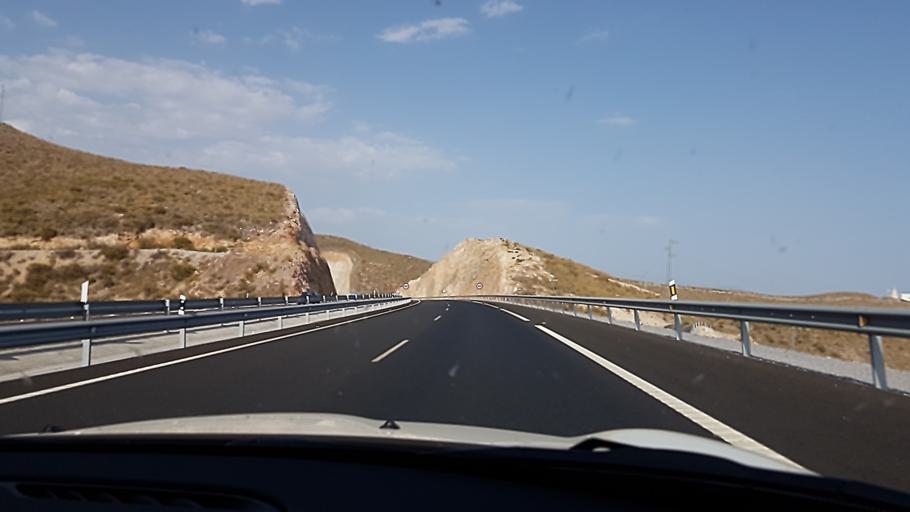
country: ES
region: Andalusia
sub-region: Provincia de Granada
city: Gualchos
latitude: 36.7167
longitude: -3.3808
